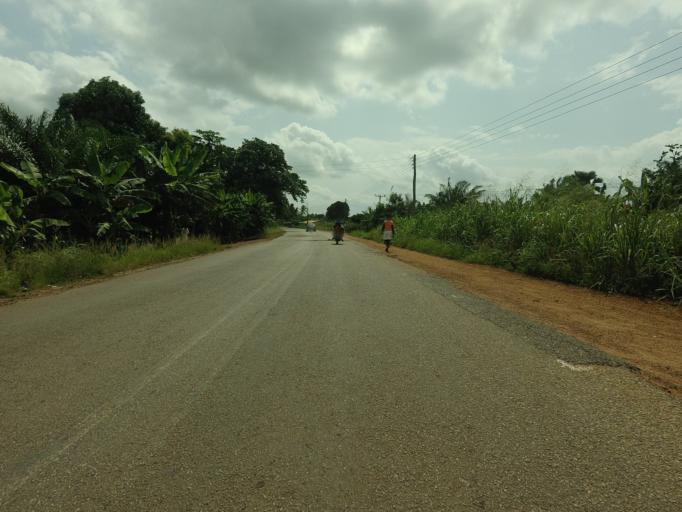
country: TG
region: Maritime
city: Lome
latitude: 6.2205
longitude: 1.0435
